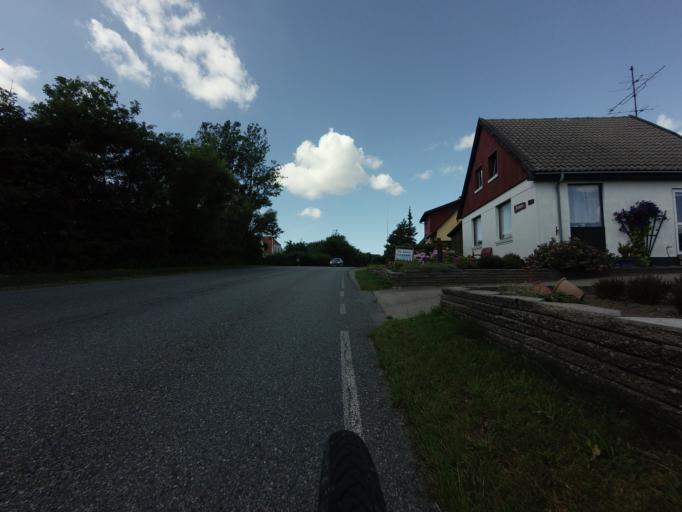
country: DK
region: North Denmark
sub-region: Hjorring Kommune
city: Hjorring
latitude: 57.4783
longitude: 9.9085
